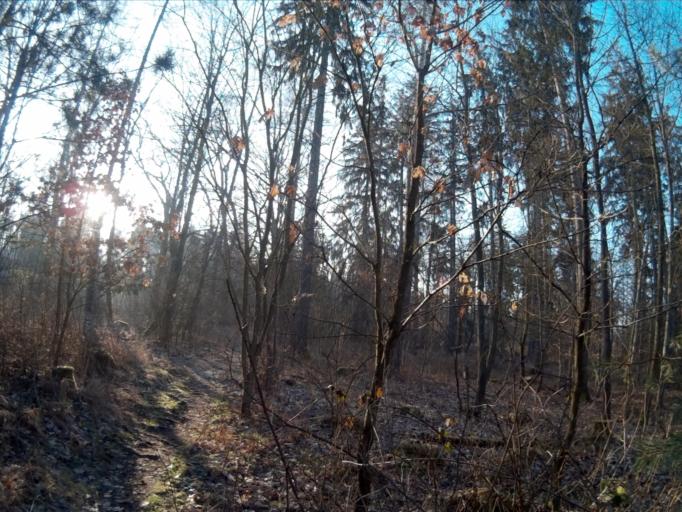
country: CZ
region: Vysocina
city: Namest' nad Oslavou
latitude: 49.1911
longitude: 16.1668
